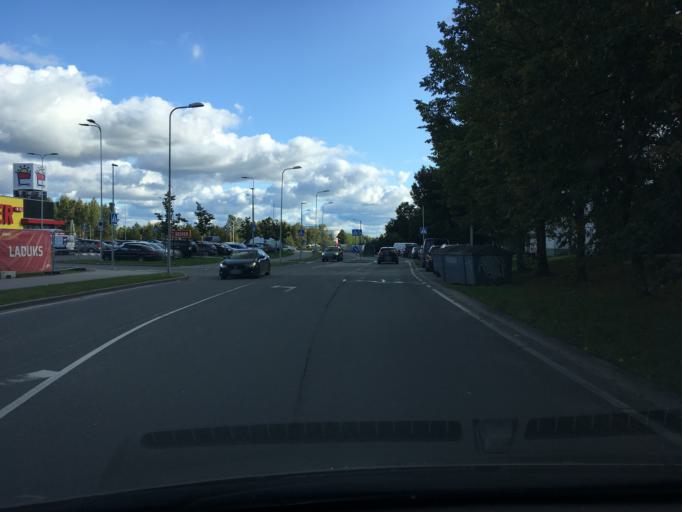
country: EE
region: Harju
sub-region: Tallinna linn
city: Kose
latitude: 59.4424
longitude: 24.8478
